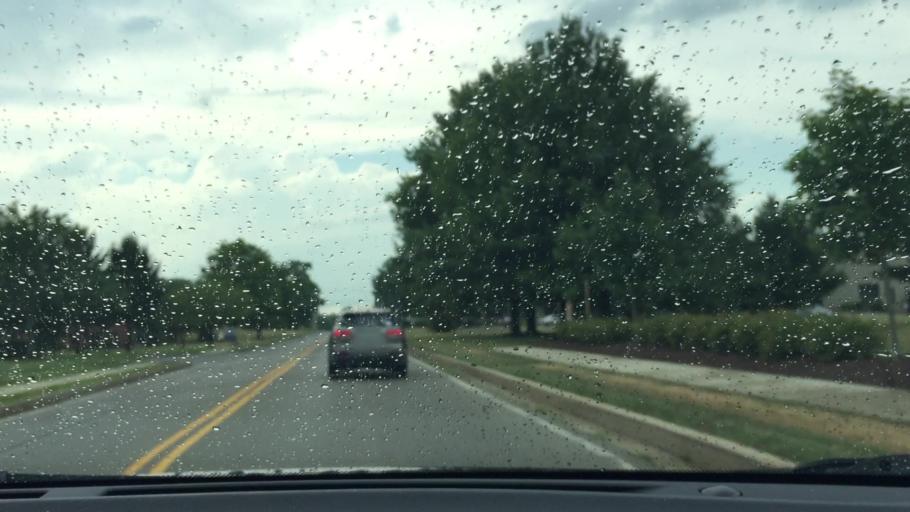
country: US
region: Pennsylvania
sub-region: Butler County
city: Cranberry Township
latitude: 40.6717
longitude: -80.1116
